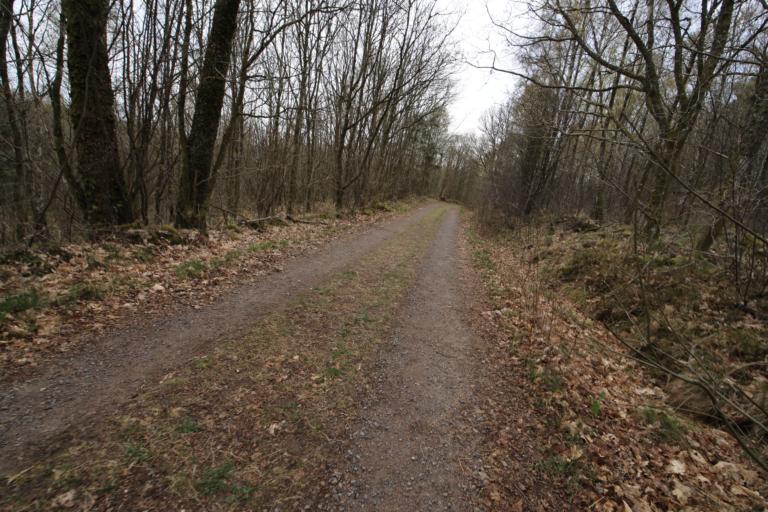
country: SE
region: Halland
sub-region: Varbergs Kommun
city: Tvaaker
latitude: 57.1509
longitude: 12.4624
